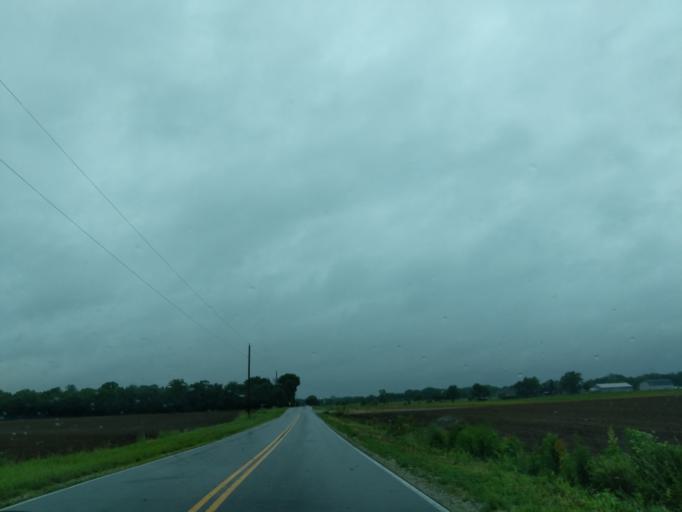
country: US
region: Indiana
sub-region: Madison County
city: Lapel
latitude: 40.0664
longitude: -85.9140
